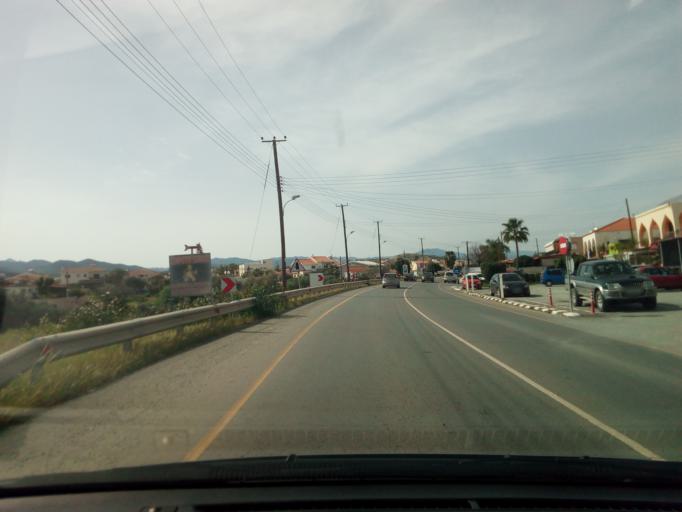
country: CY
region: Lefkosia
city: Arediou
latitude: 35.0529
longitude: 33.2024
